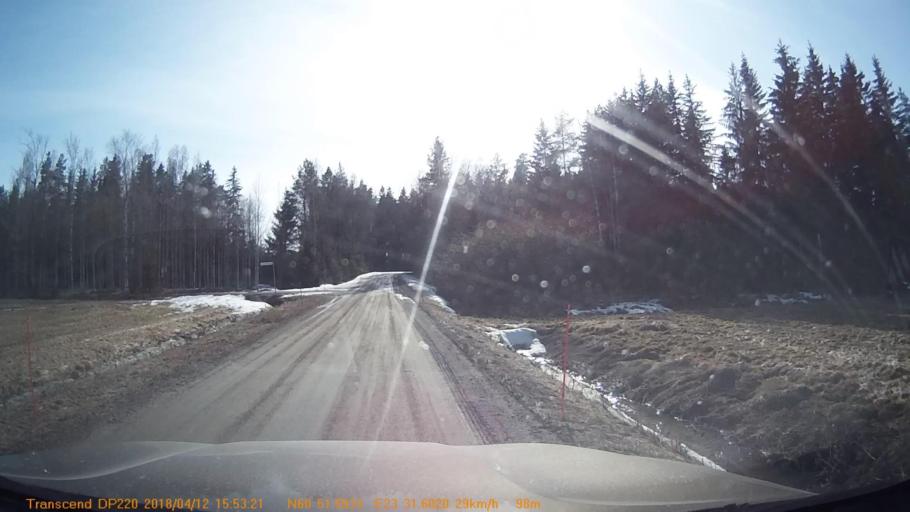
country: FI
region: Haeme
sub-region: Forssa
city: Jokioinen
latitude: 60.8598
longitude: 23.5266
